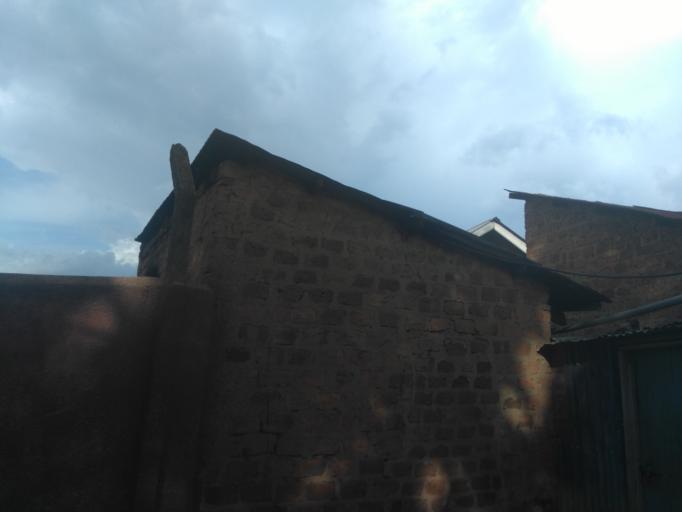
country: UG
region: Central Region
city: Kampala Central Division
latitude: 0.3580
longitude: 32.5812
